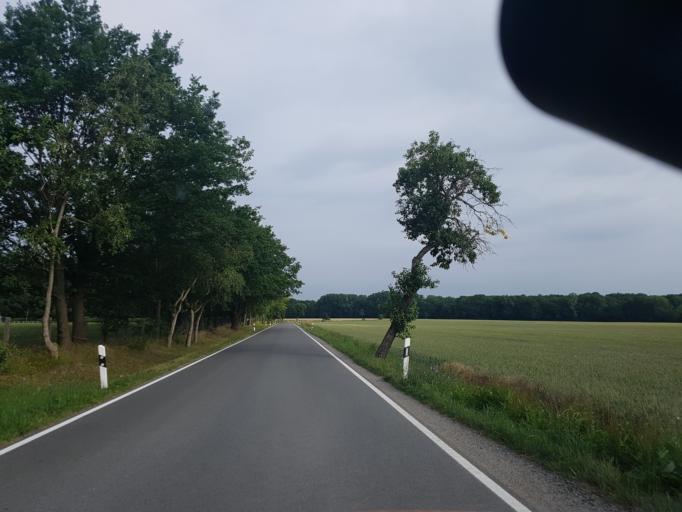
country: DE
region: Brandenburg
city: Sonnewalde
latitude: 51.6917
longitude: 13.6283
